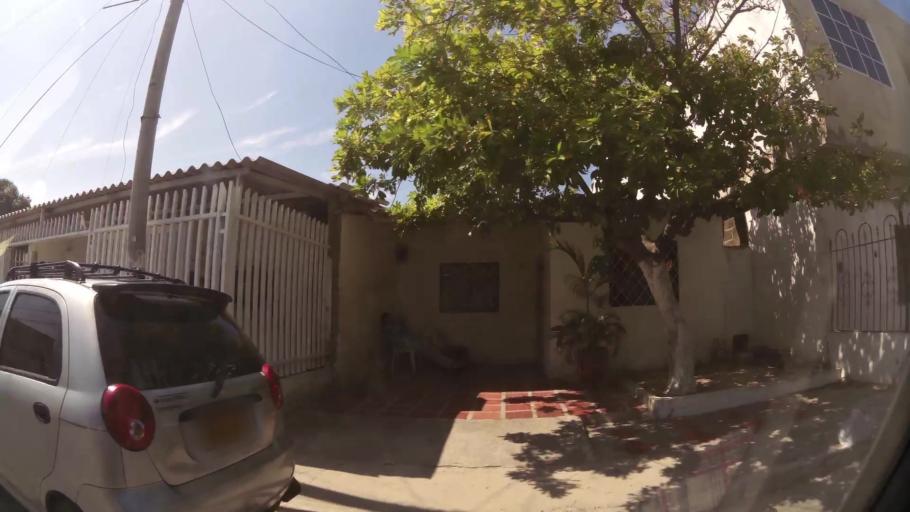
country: CO
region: Atlantico
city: Barranquilla
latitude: 10.9772
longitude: -74.8410
